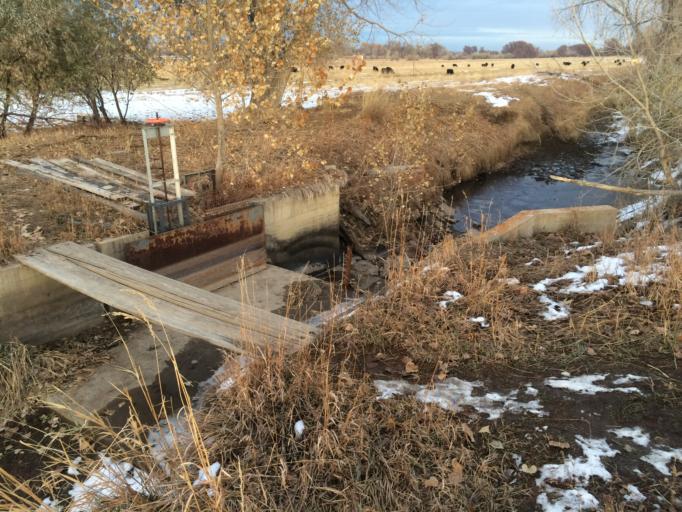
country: US
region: Colorado
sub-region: Boulder County
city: Gunbarrel
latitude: 40.0315
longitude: -105.1473
